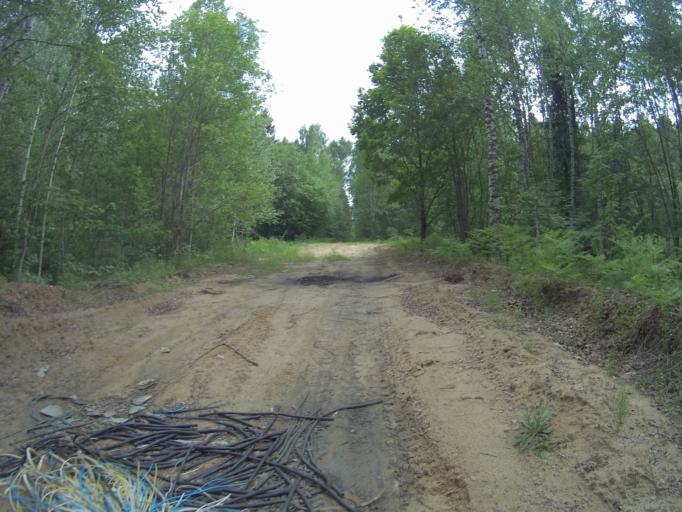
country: RU
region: Vladimir
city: Raduzhnyy
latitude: 55.9894
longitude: 40.2736
